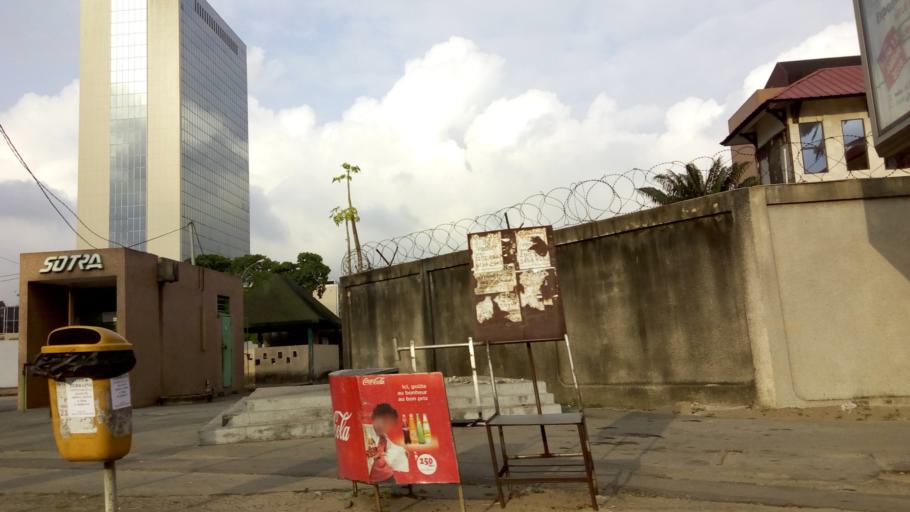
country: CI
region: Lagunes
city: Abidjan
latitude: 5.3306
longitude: -4.0239
